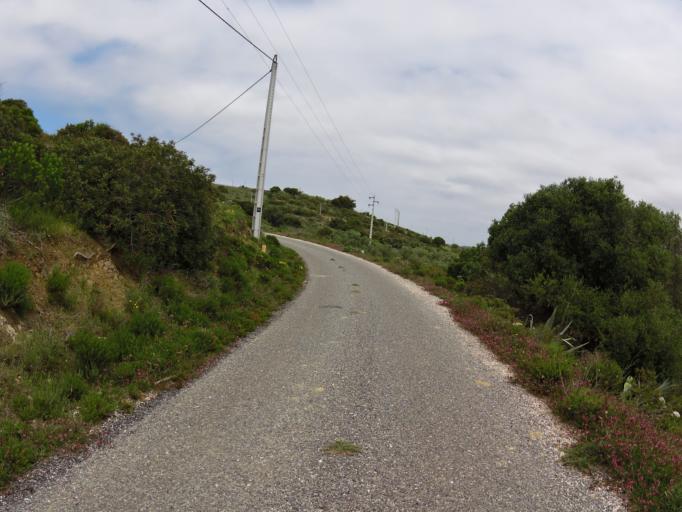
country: PT
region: Faro
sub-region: Vila do Bispo
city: Vila do Bispo
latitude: 37.0766
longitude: -8.8758
